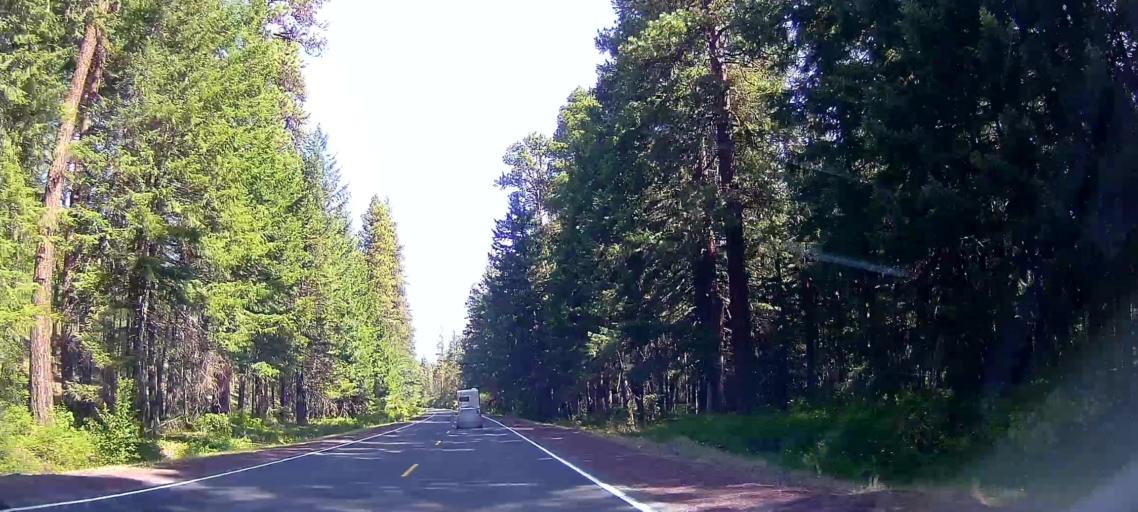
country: US
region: Oregon
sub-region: Jefferson County
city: Warm Springs
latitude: 45.0502
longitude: -121.5107
